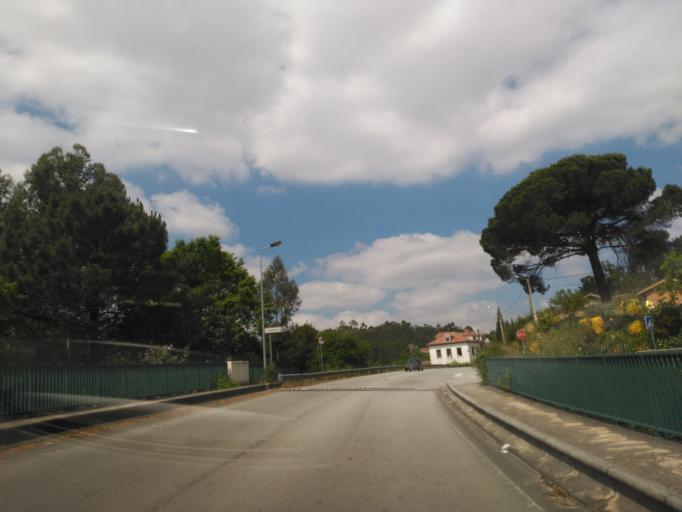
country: PT
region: Braga
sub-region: Braga
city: Oliveira
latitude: 41.5194
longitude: -8.4694
